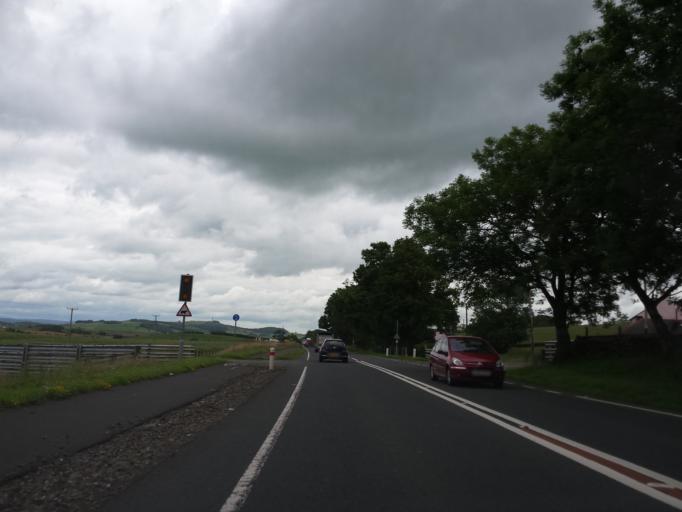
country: GB
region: Scotland
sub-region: Dumfries and Galloway
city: Dalbeattie
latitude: 55.0451
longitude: -3.7932
